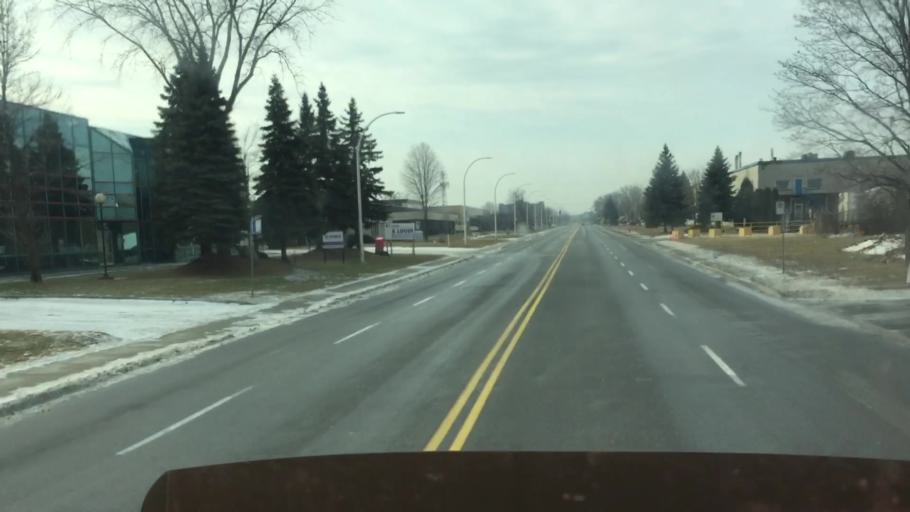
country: CA
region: Quebec
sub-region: Montreal
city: Pointe-Claire
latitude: 45.4747
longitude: -73.7933
